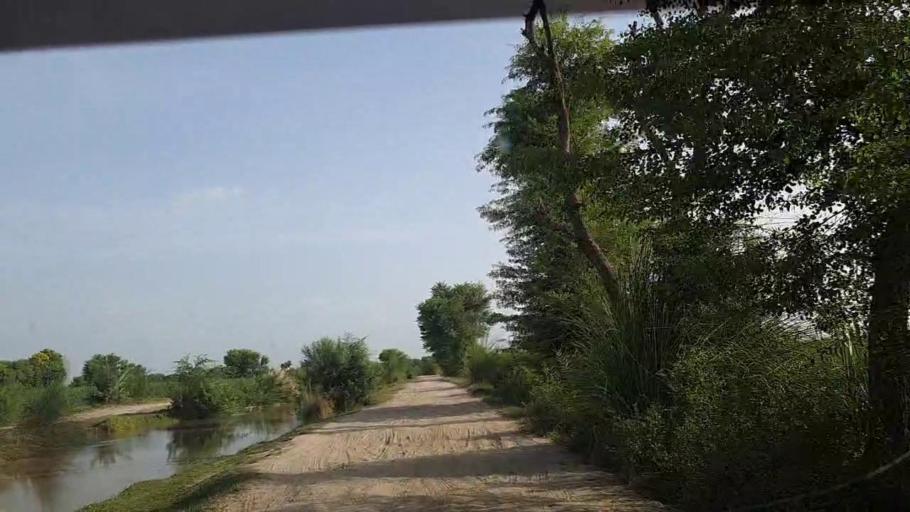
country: PK
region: Sindh
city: Ghotki
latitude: 27.9988
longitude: 69.2617
